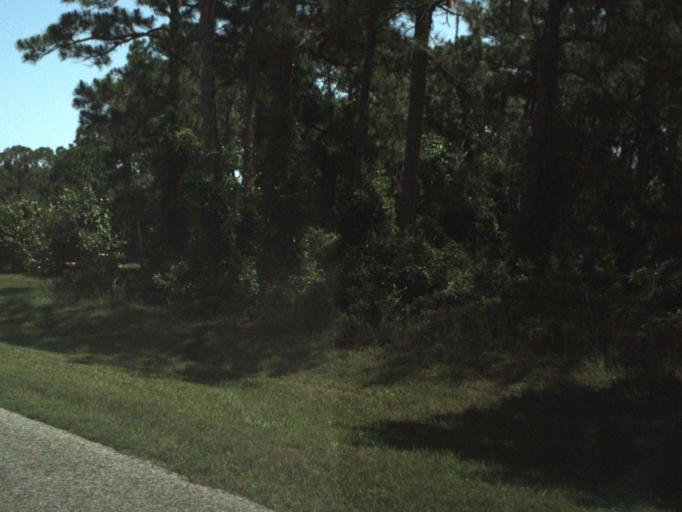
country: US
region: Florida
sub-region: Brevard County
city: Sharpes
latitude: 28.4509
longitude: -80.7091
